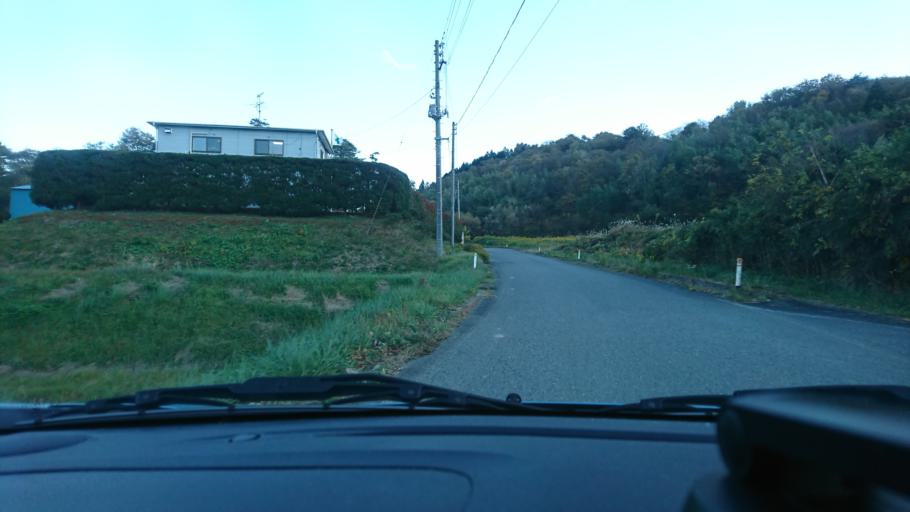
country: JP
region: Iwate
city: Ichinoseki
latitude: 38.7691
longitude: 141.2298
